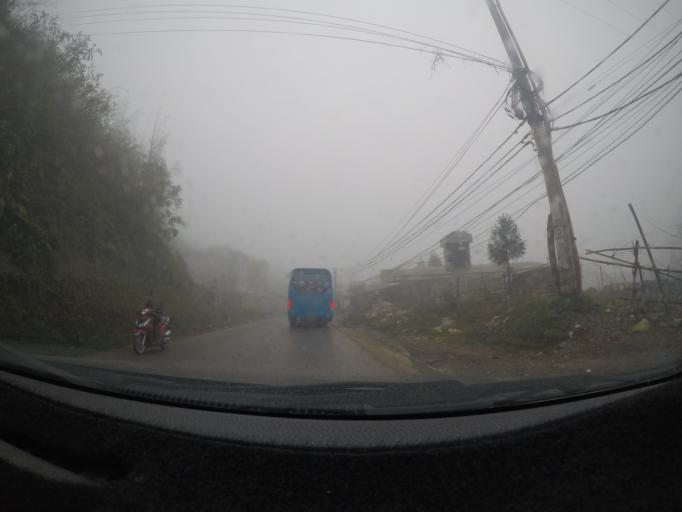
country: VN
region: Lao Cai
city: Sa Pa
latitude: 22.3407
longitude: 103.8411
